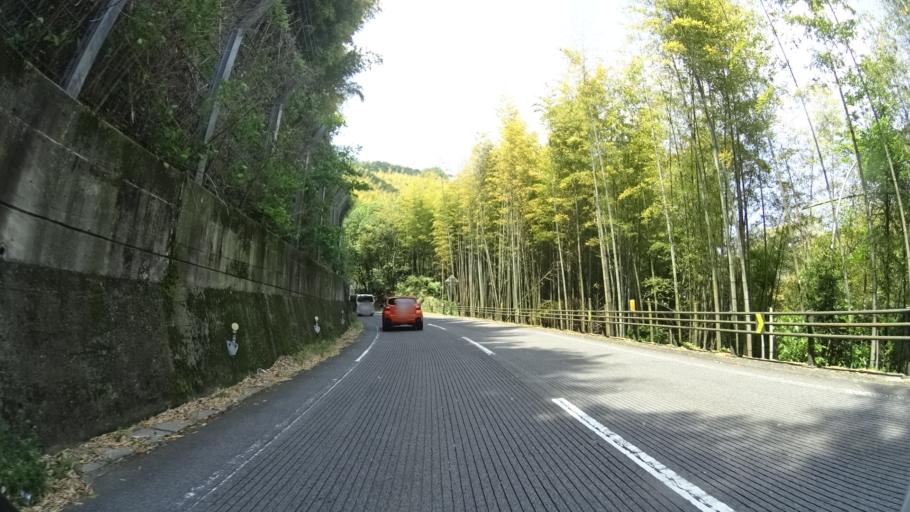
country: JP
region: Ehime
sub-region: Shikoku-chuo Shi
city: Matsuyama
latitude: 33.8772
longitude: 132.8361
